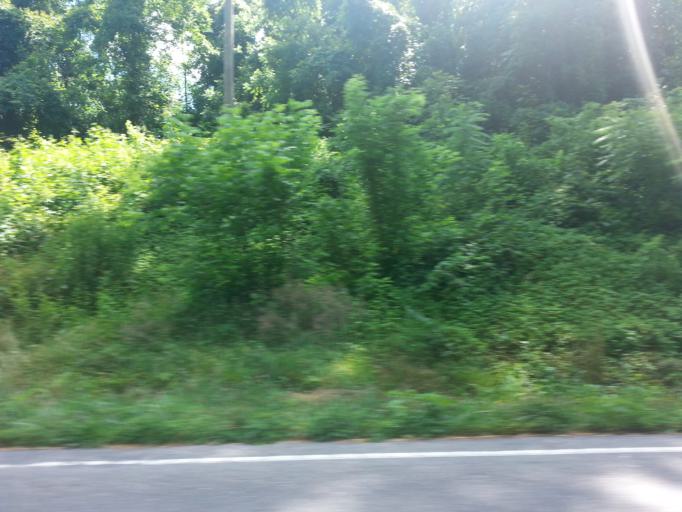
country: US
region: Virginia
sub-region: Lee County
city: Pennington Gap
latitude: 36.7650
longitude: -83.0240
